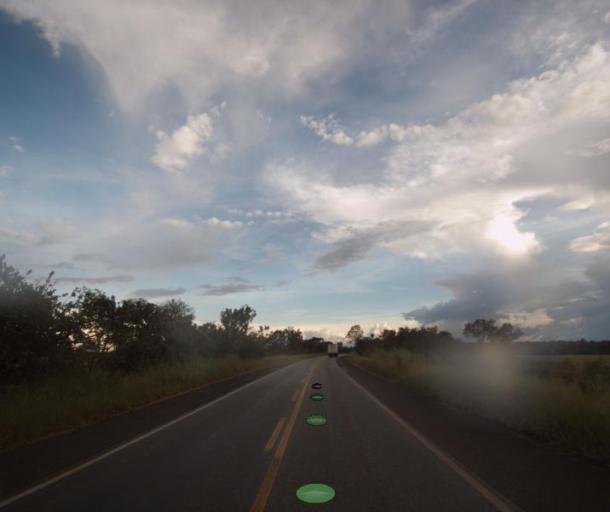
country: BR
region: Goias
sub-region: Uruacu
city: Uruacu
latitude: -14.0434
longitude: -49.0884
